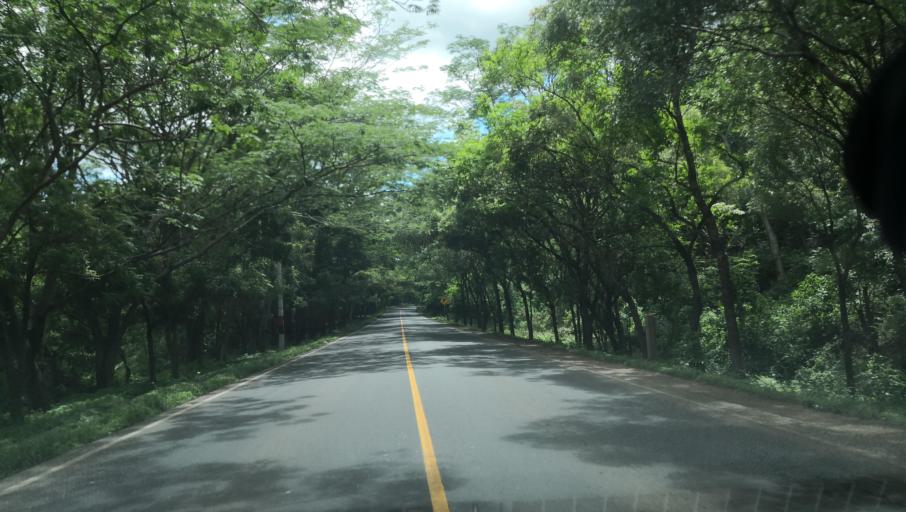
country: NI
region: Madriz
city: Yalaguina
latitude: 13.4768
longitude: -86.4837
